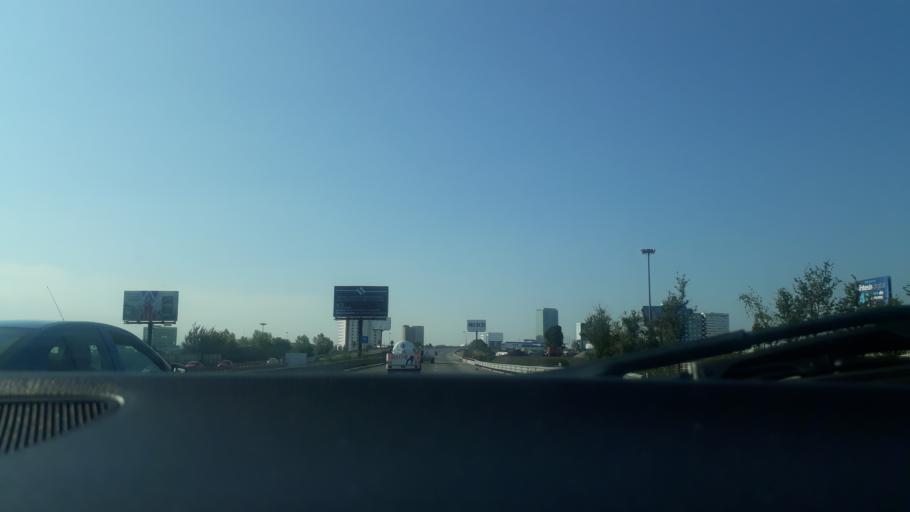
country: MX
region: Puebla
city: Tlazcalancingo
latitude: 19.0095
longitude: -98.2612
